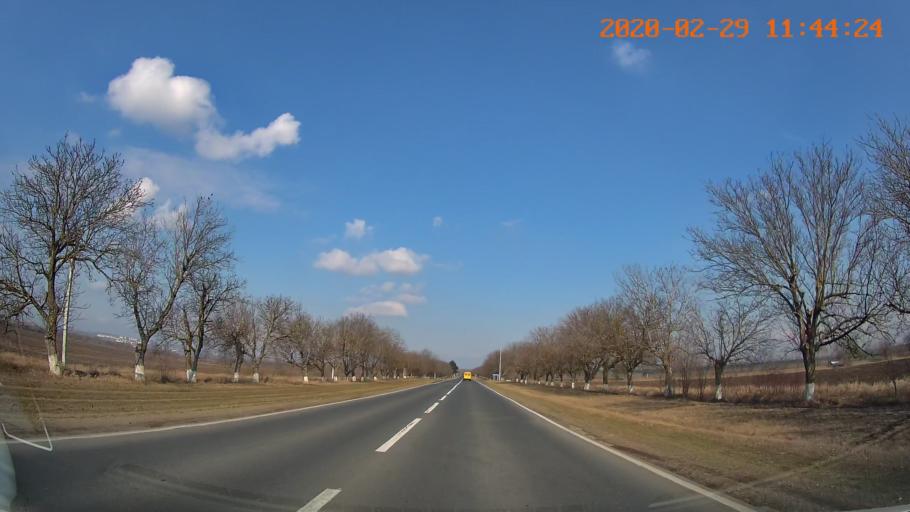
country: MD
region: Rezina
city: Saharna
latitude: 47.7109
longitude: 29.0008
